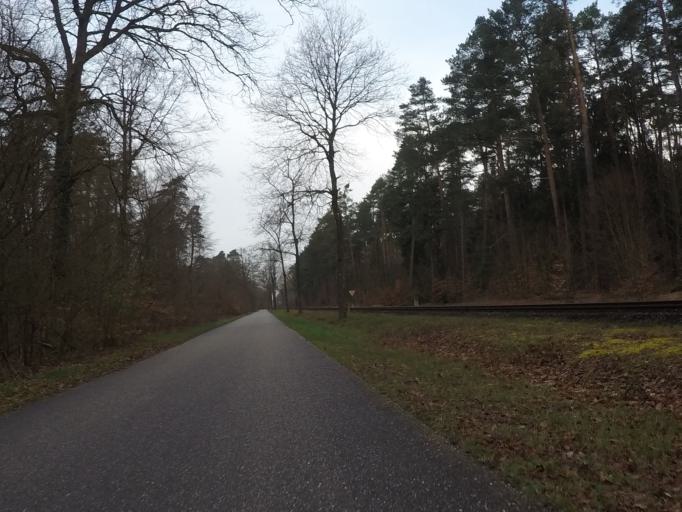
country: DE
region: Rheinland-Pfalz
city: Kandel
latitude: 49.0705
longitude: 8.2209
